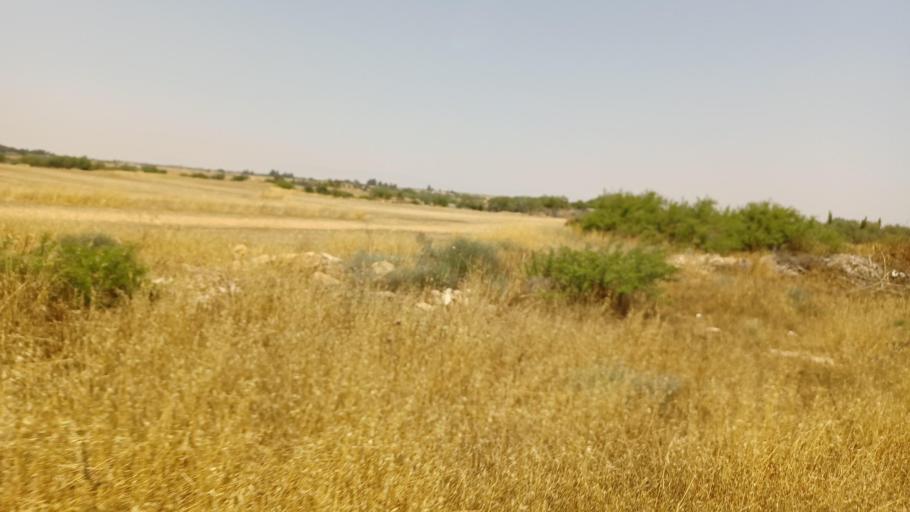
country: CY
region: Ammochostos
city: Avgorou
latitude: 35.0568
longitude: 33.8419
